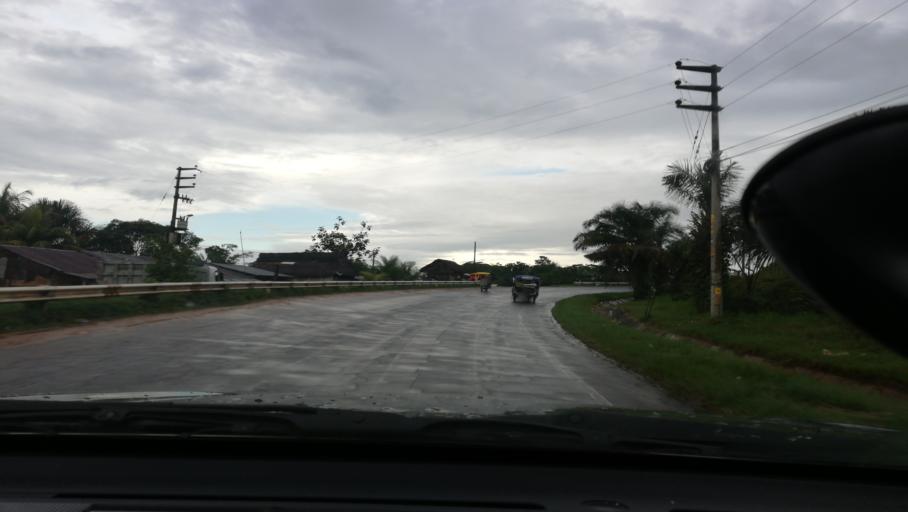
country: PE
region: Loreto
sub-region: Provincia de Maynas
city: Iquitos
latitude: -3.8944
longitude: -73.3484
